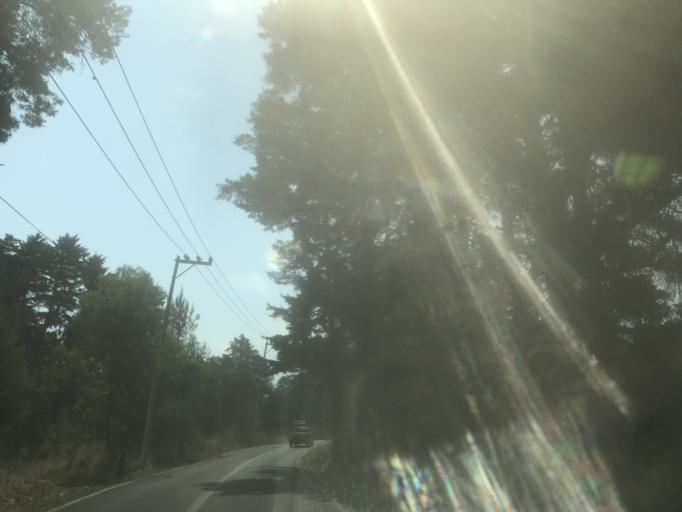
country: MX
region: Mexico
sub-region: Atlautla
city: San Juan Tepecoculco
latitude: 18.9982
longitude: -98.7758
